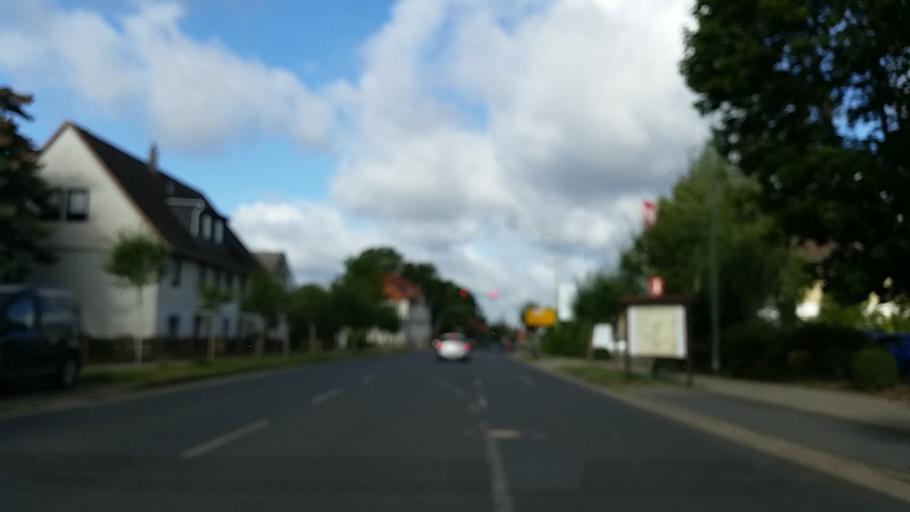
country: DE
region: Lower Saxony
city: Cremlingen
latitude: 52.2482
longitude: 10.6566
